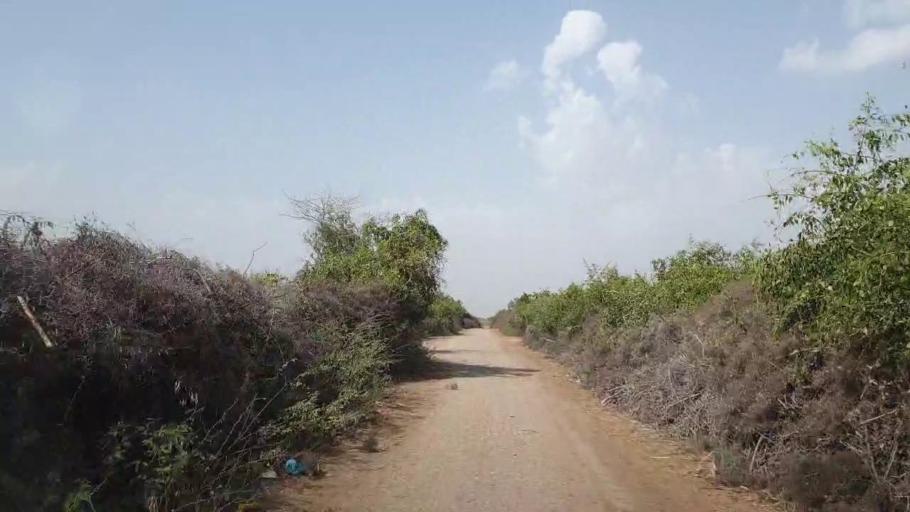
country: PK
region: Sindh
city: Rajo Khanani
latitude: 25.0350
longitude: 68.8831
